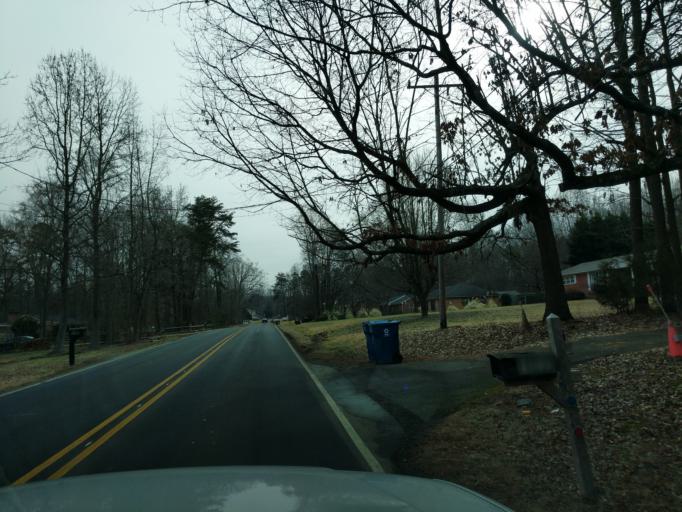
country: US
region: North Carolina
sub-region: Mecklenburg County
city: Huntersville
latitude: 35.3190
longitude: -80.8901
